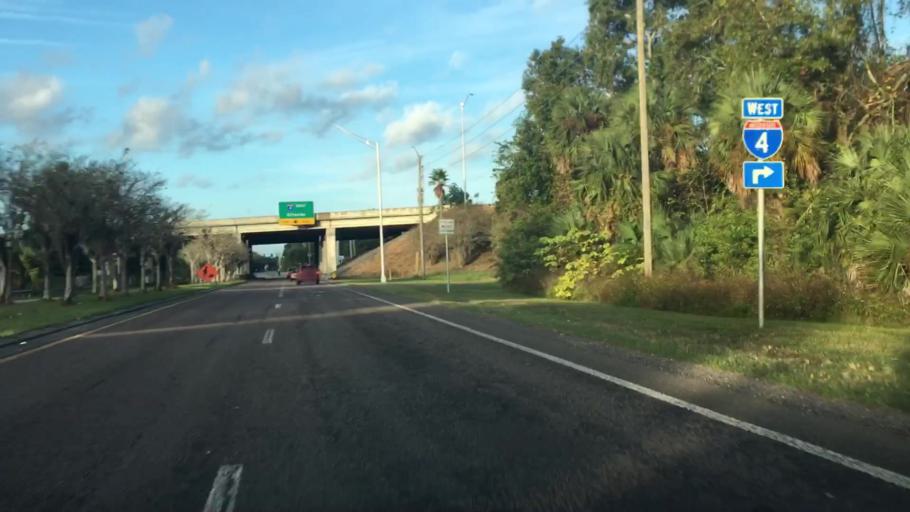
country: US
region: Florida
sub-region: Volusia County
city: DeBary
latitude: 28.8722
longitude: -81.2828
